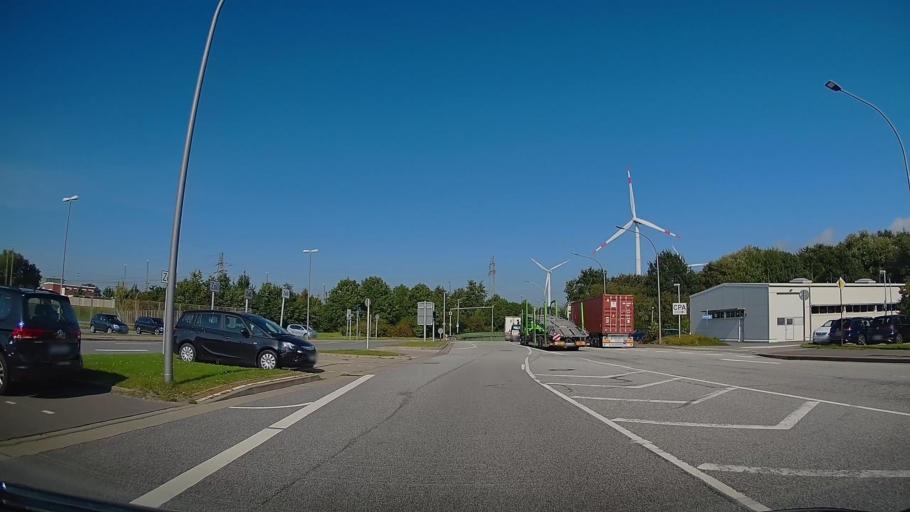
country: DE
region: Lower Saxony
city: Langen
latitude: 53.5958
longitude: 8.5395
